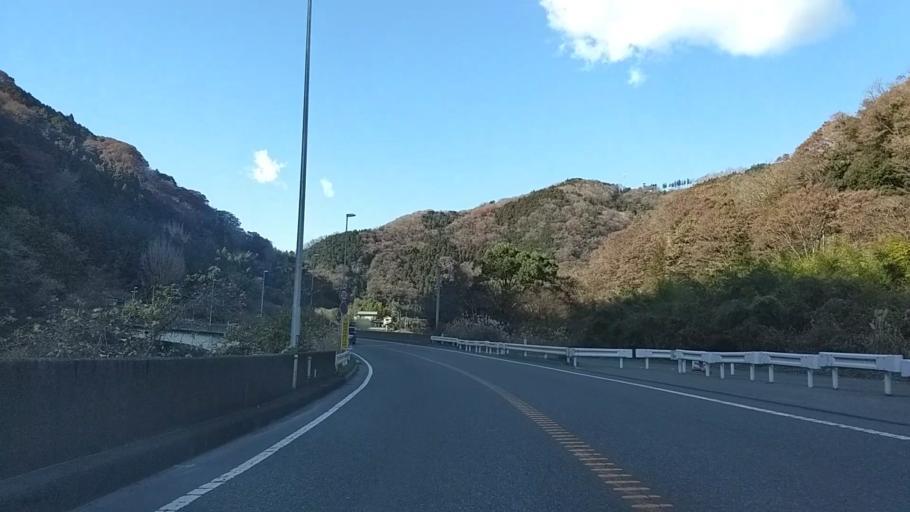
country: JP
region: Shizuoka
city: Gotemba
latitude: 35.3598
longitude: 139.0584
